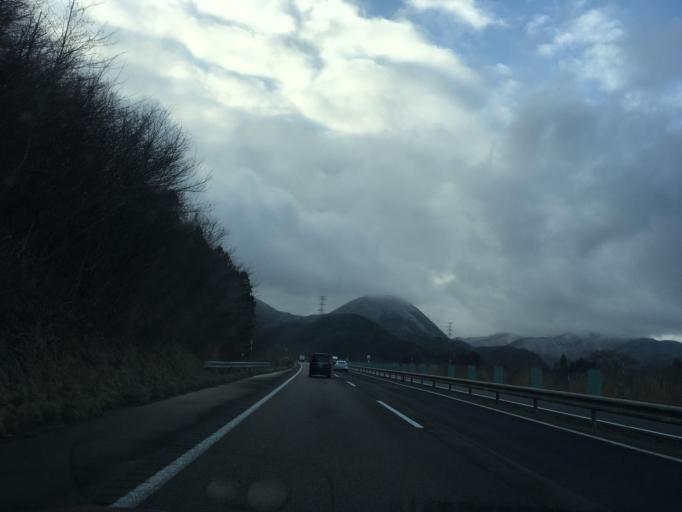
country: JP
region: Miyagi
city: Shiroishi
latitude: 38.1823
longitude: 140.6052
